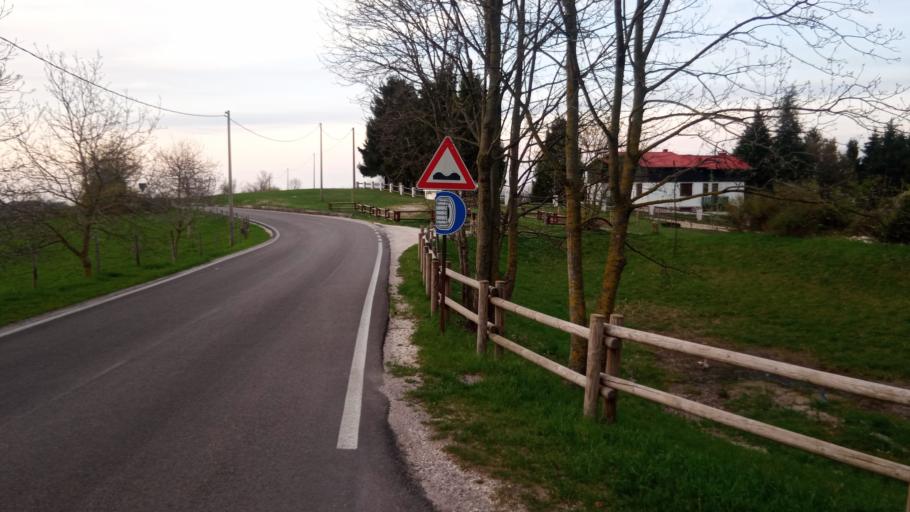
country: IT
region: Veneto
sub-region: Provincia di Vicenza
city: Conco
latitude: 45.8024
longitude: 11.6231
